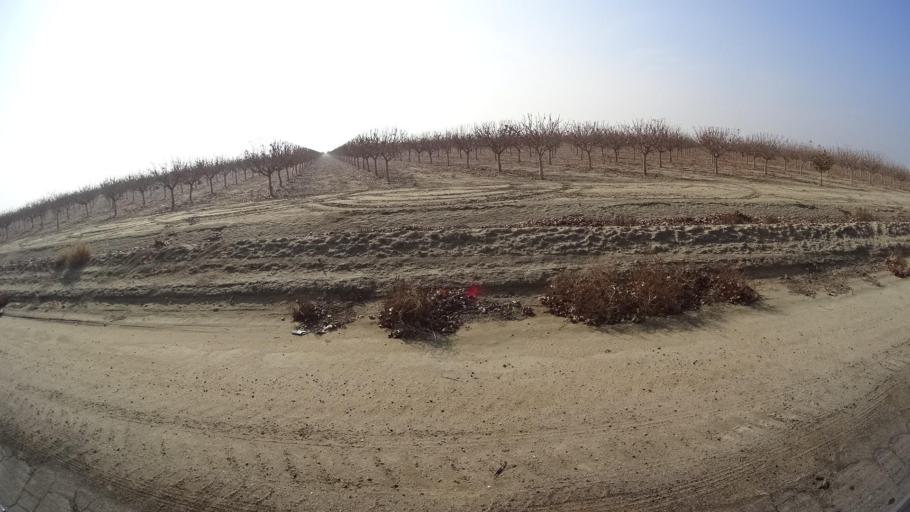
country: US
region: California
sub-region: Kern County
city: Buttonwillow
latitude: 35.4420
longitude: -119.4595
